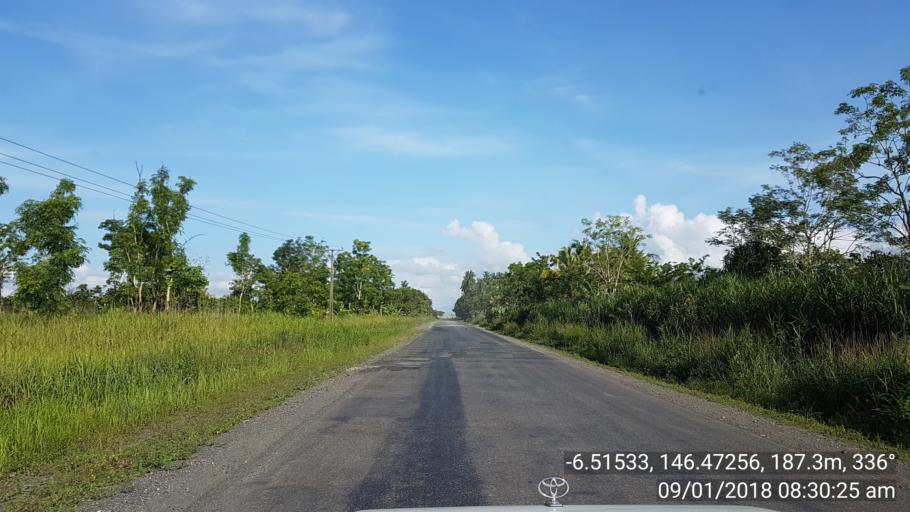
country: PG
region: Morobe
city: Lae
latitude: -6.5152
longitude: 146.4726
